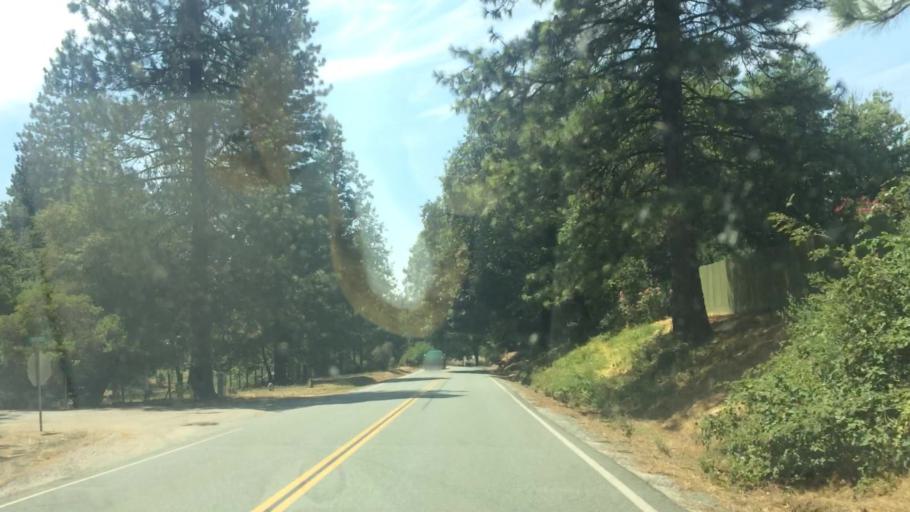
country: US
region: California
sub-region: Amador County
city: Pine Grove
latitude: 38.4141
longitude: -120.6823
